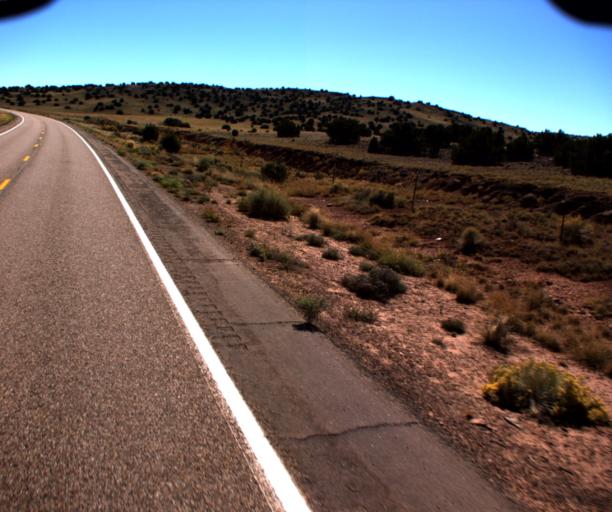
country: US
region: Arizona
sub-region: Apache County
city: Saint Johns
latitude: 34.5718
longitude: -109.5243
